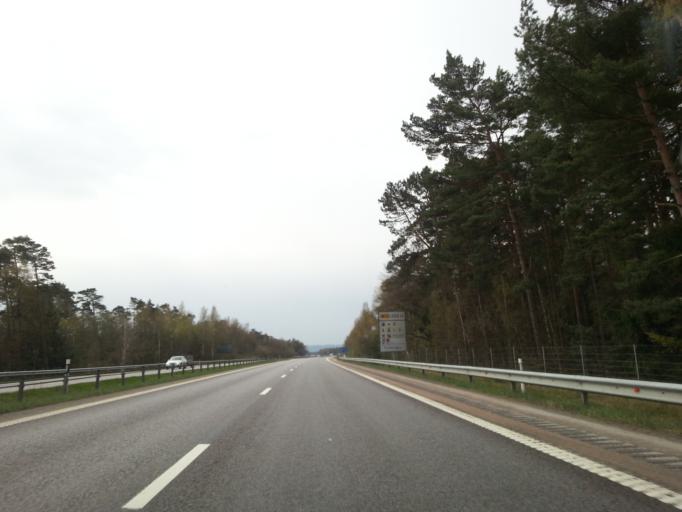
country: SE
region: Halland
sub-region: Laholms Kommun
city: Mellbystrand
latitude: 56.5134
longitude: 12.9637
